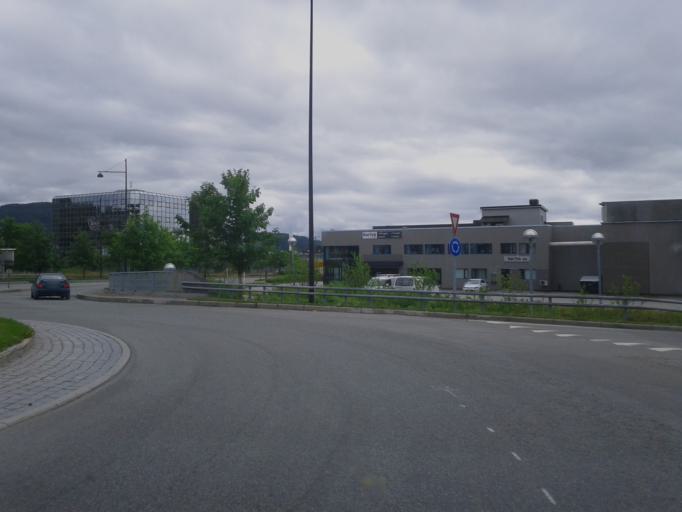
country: NO
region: Nord-Trondelag
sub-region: Steinkjer
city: Steinkjer
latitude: 64.0211
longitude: 11.4905
